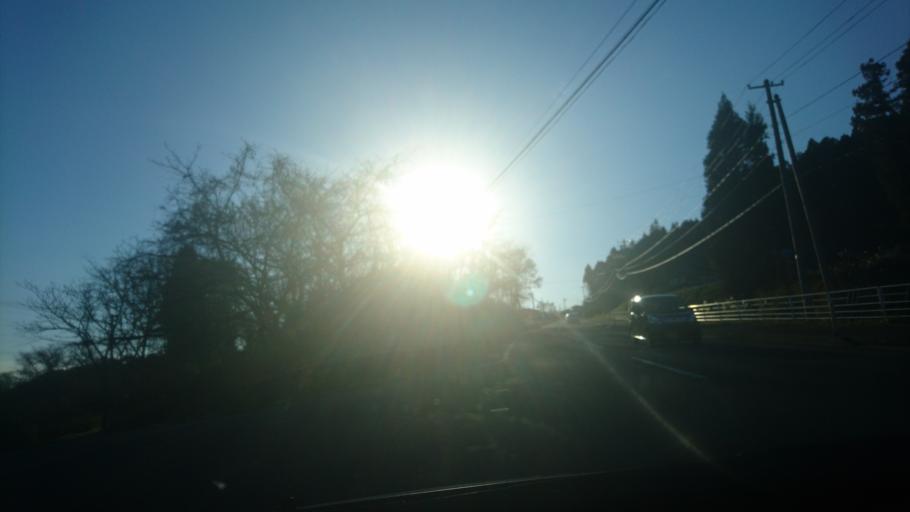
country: JP
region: Iwate
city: Ichinoseki
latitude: 38.9009
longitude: 141.2066
